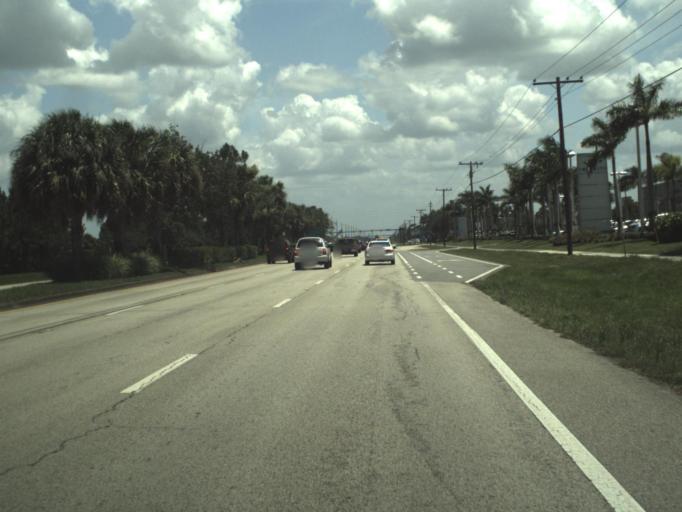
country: US
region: Florida
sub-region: Martin County
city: Port Salerno
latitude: 27.1579
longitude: -80.2222
